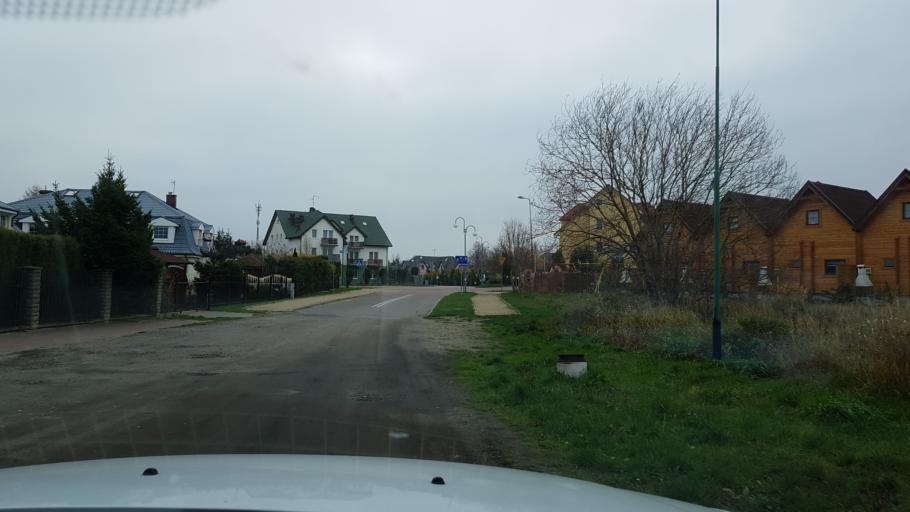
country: PL
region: West Pomeranian Voivodeship
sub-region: Powiat gryficki
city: Rewal
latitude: 54.0826
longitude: 15.0286
